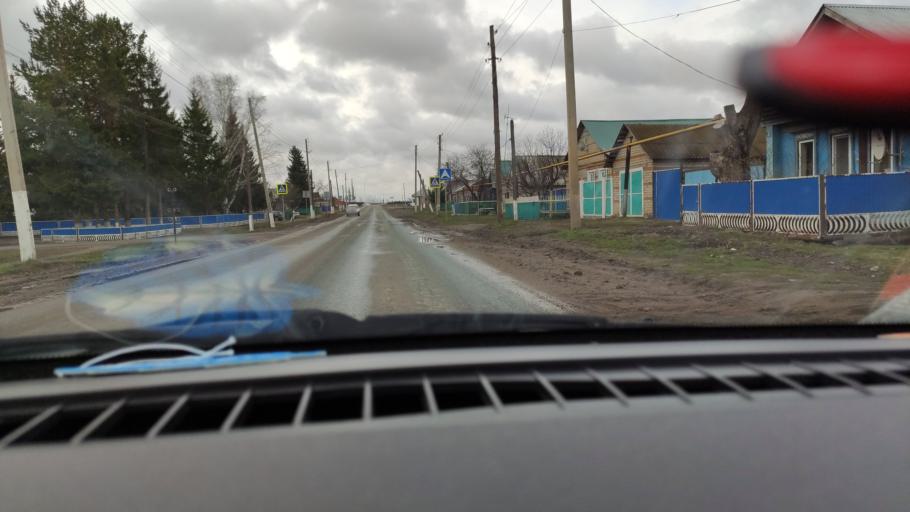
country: RU
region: Tatarstan
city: Cheremshan
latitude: 54.9265
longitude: 51.6827
